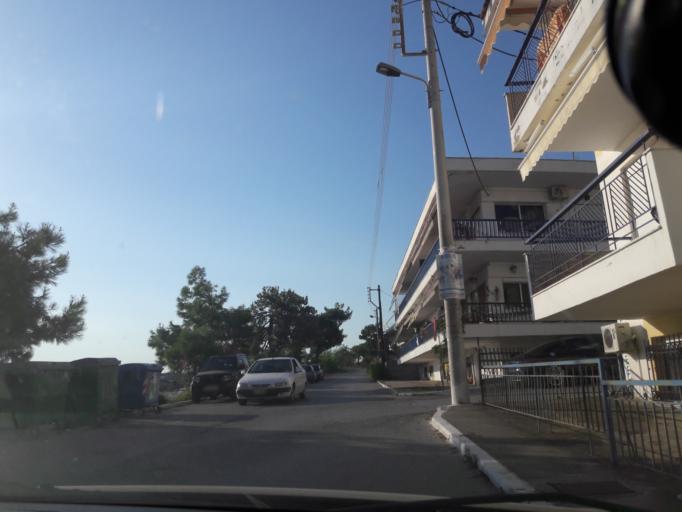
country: GR
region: Central Macedonia
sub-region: Nomos Chalkidikis
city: Nea Kallikrateia
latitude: 40.3451
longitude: 23.0137
